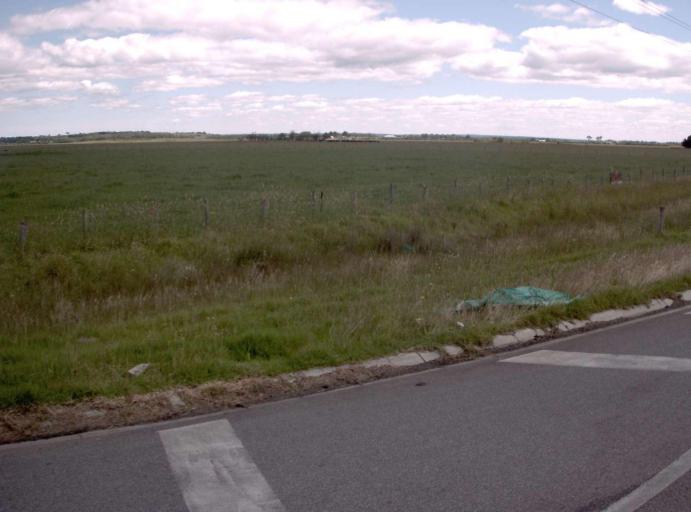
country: AU
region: Victoria
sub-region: Bass Coast
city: North Wonthaggi
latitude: -38.4721
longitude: 145.4749
